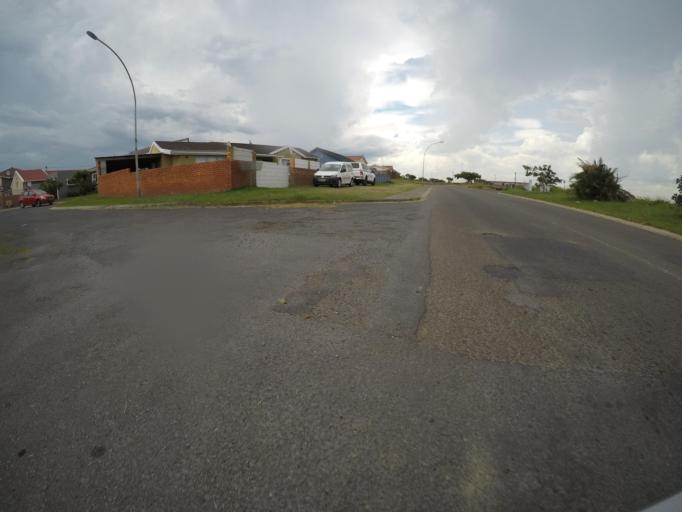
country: ZA
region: Eastern Cape
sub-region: Buffalo City Metropolitan Municipality
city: East London
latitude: -33.0220
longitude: 27.8579
